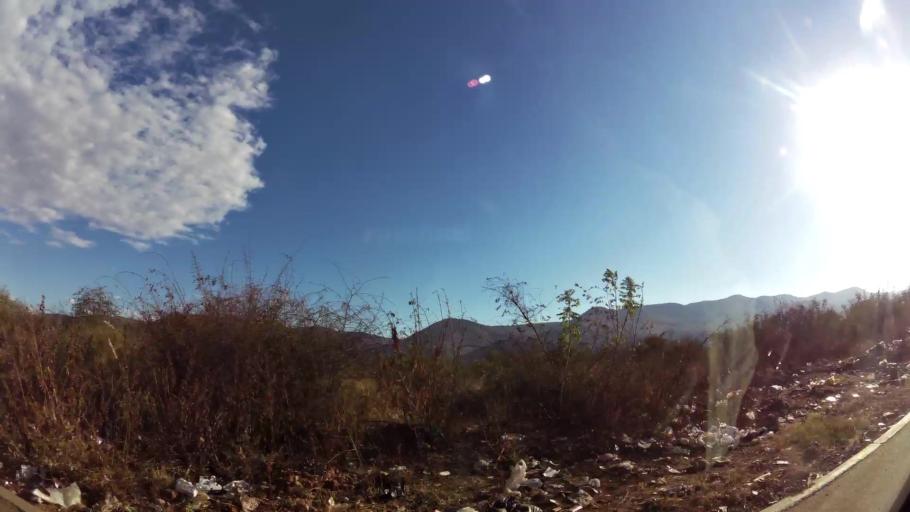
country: ZA
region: Limpopo
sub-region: Waterberg District Municipality
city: Mokopane
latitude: -24.1911
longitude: 28.9798
